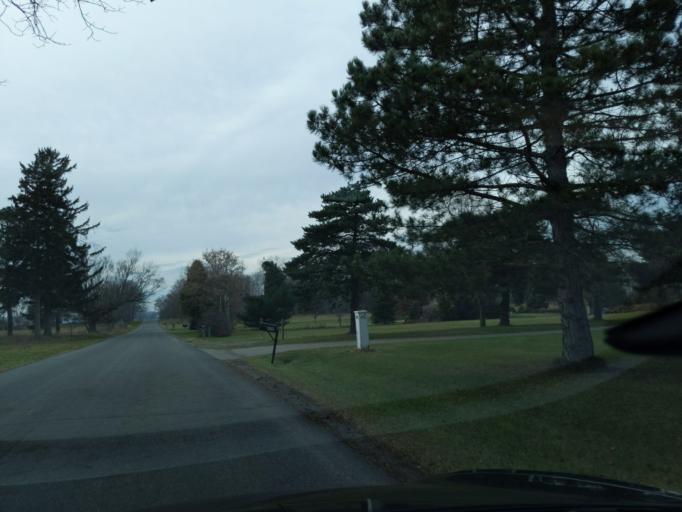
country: US
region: Michigan
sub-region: Ingham County
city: Okemos
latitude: 42.6544
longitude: -84.3708
